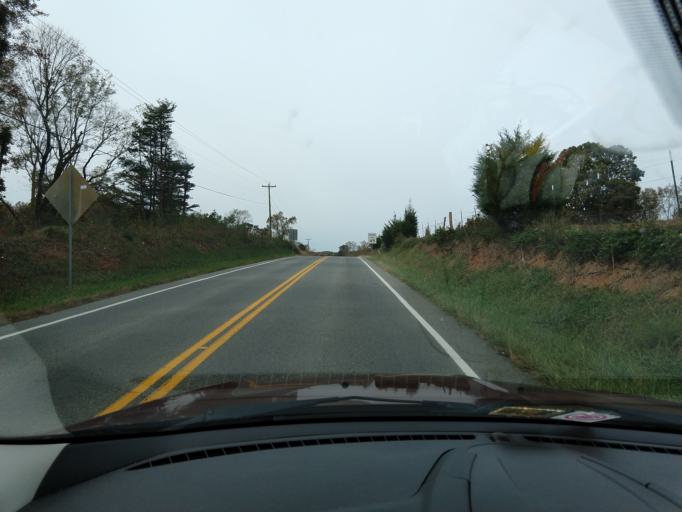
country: US
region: Virginia
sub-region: Franklin County
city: Union Hall
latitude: 36.9925
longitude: -79.6782
